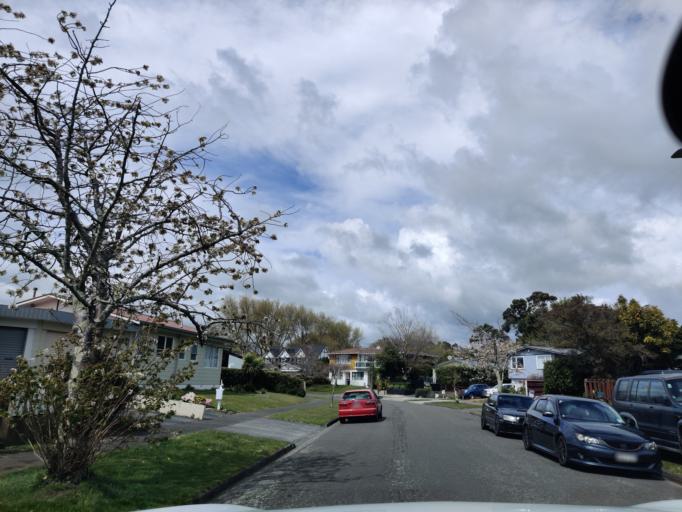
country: NZ
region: Manawatu-Wanganui
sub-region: Palmerston North City
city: Palmerston North
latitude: -40.3810
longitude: 175.5906
